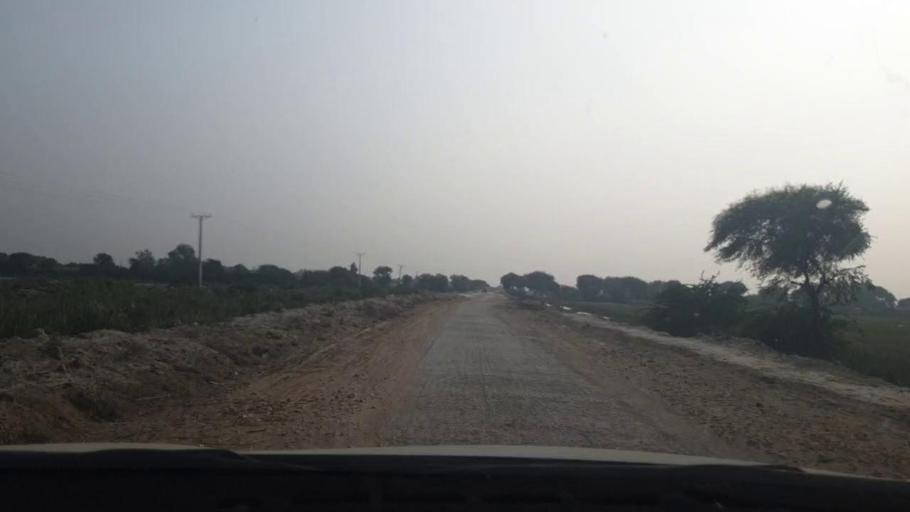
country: PK
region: Sindh
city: Bulri
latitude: 24.7906
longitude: 68.4263
